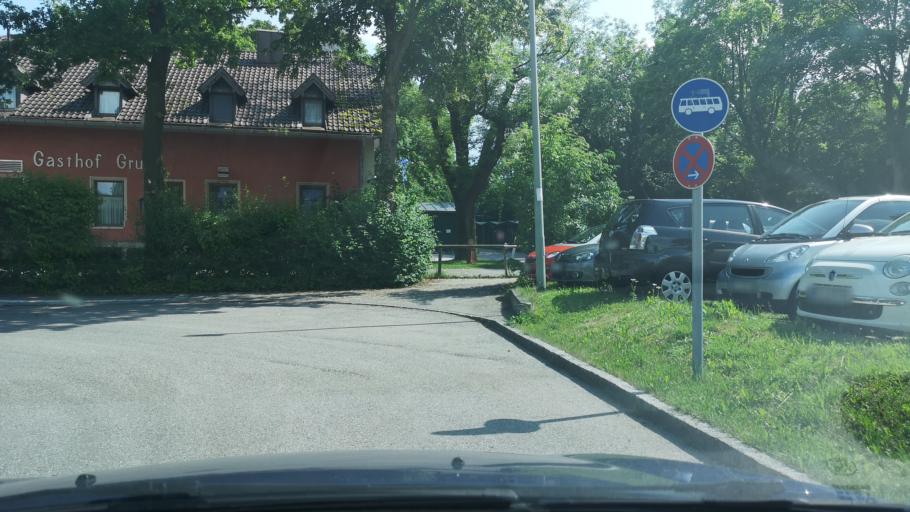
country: DE
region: Bavaria
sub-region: Upper Bavaria
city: Kirchheim bei Muenchen
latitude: 48.1654
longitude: 11.7822
